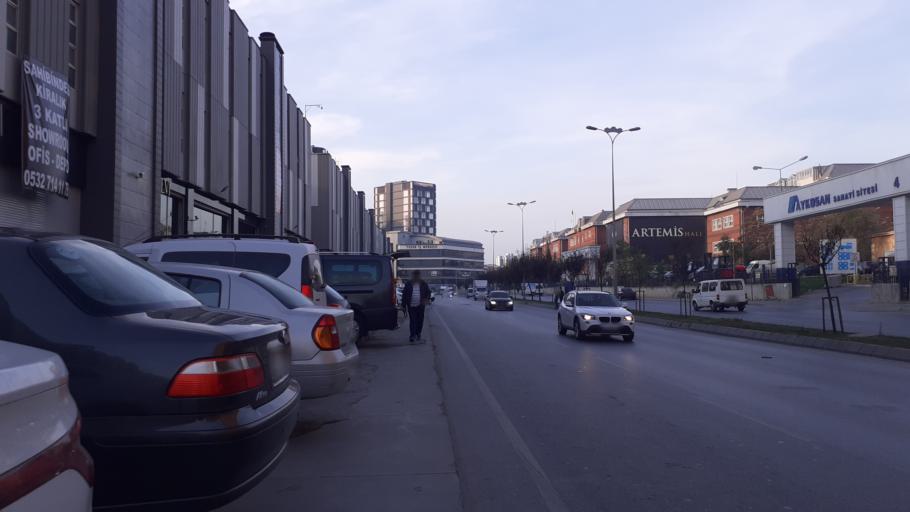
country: TR
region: Istanbul
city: Basaksehir
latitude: 41.0708
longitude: 28.7953
